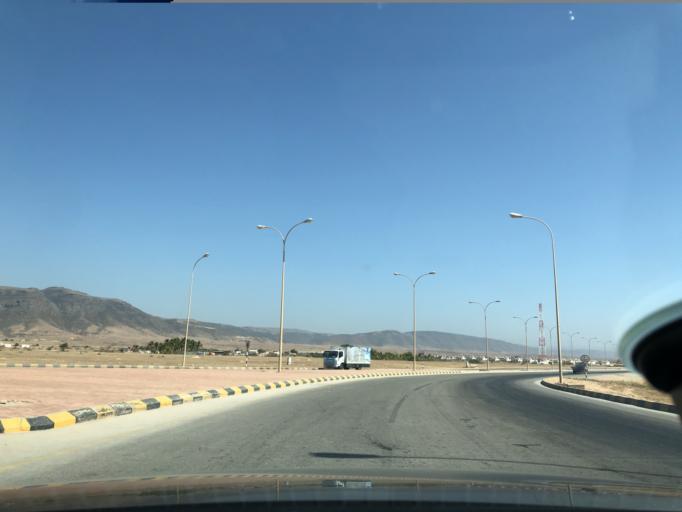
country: OM
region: Zufar
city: Salalah
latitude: 17.0532
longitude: 54.2754
